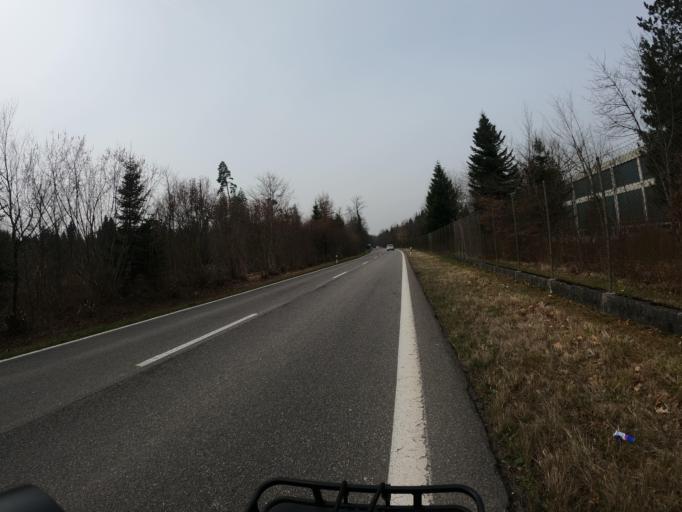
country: CH
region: Aargau
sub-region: Bezirk Brugg
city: Rupperswil
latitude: 47.4055
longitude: 8.1059
